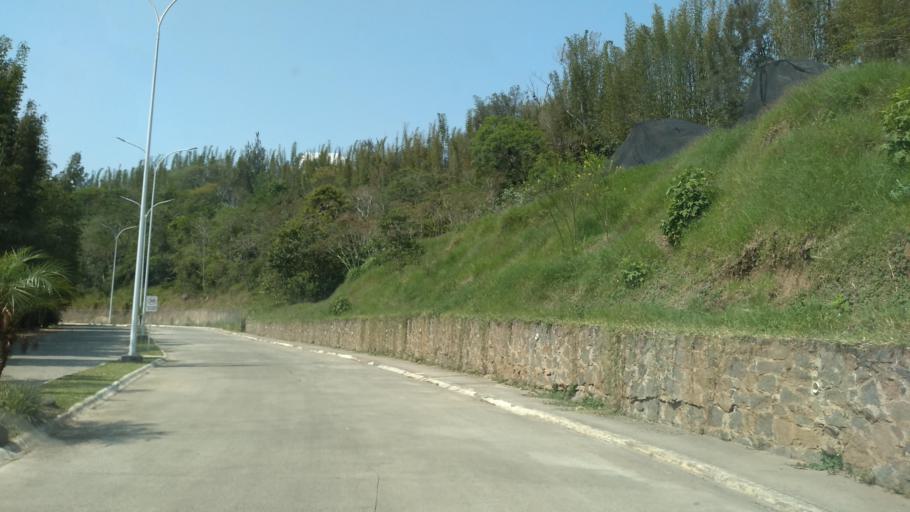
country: MX
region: Veracruz
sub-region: Emiliano Zapata
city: Las Trancas
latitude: 19.5254
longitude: -96.8635
